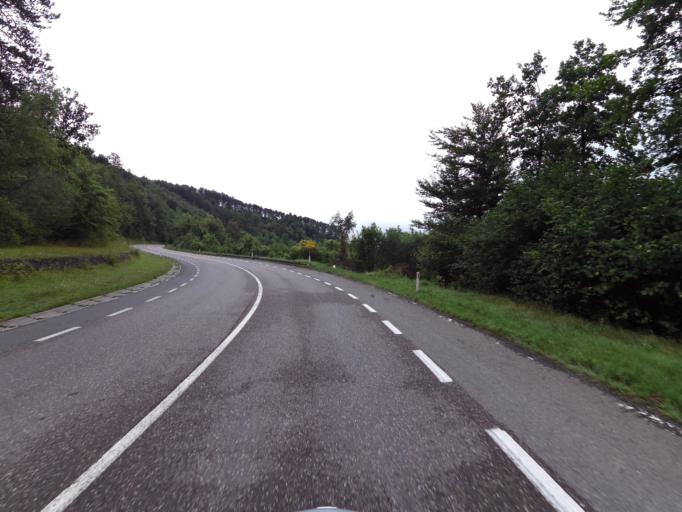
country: BE
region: Wallonia
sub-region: Province de Namur
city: Rochefort
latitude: 50.1423
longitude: 5.1850
